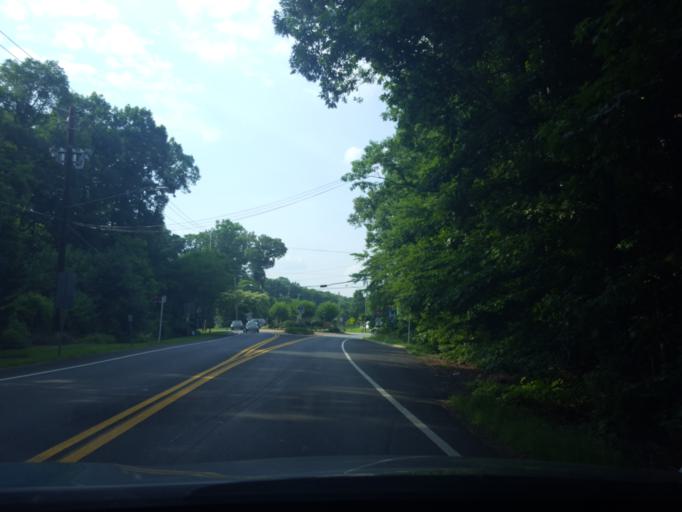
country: US
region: Maryland
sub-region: Prince George's County
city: Fort Washington
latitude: 38.7239
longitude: -77.0047
